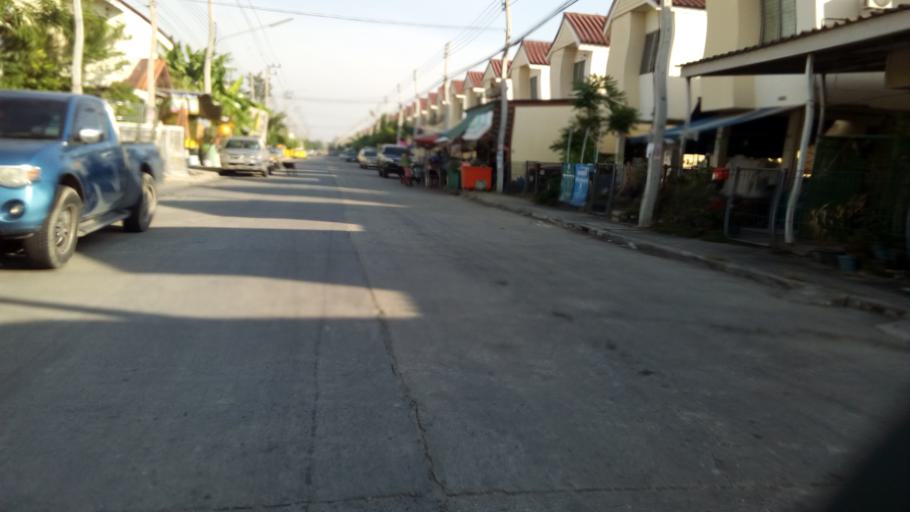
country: TH
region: Pathum Thani
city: Nong Suea
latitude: 14.0528
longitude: 100.8414
